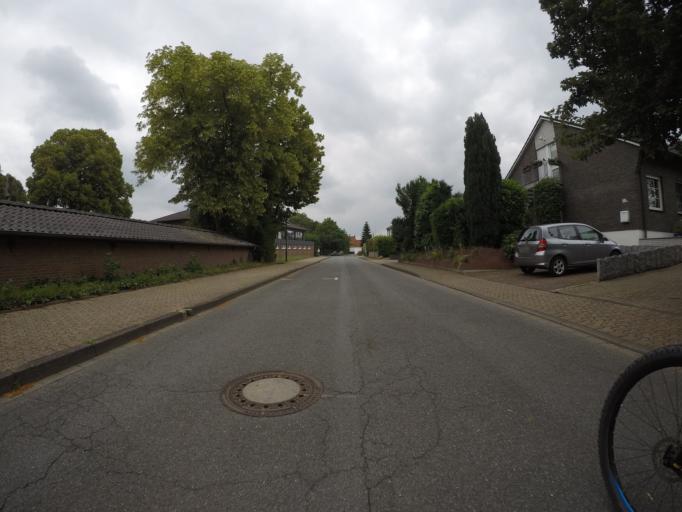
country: DE
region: North Rhine-Westphalia
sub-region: Regierungsbezirk Dusseldorf
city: Wesel
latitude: 51.7253
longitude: 6.6760
